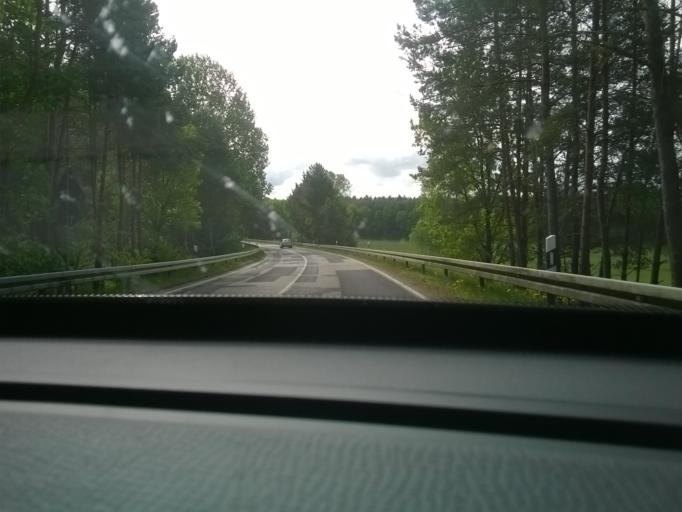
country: DE
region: Brandenburg
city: Wittstock
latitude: 53.1021
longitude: 12.4831
